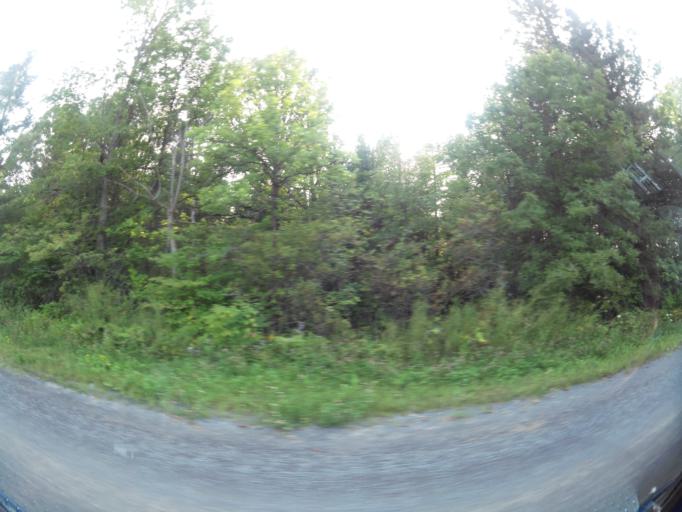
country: CA
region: Ontario
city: Clarence-Rockland
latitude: 45.4853
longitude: -75.4628
